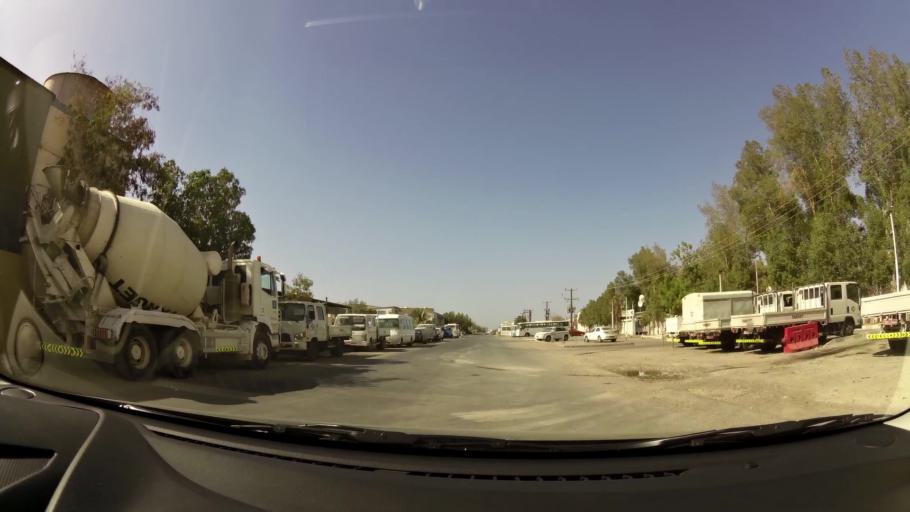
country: OM
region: Muhafazat Masqat
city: Bawshar
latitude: 23.5697
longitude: 58.3570
